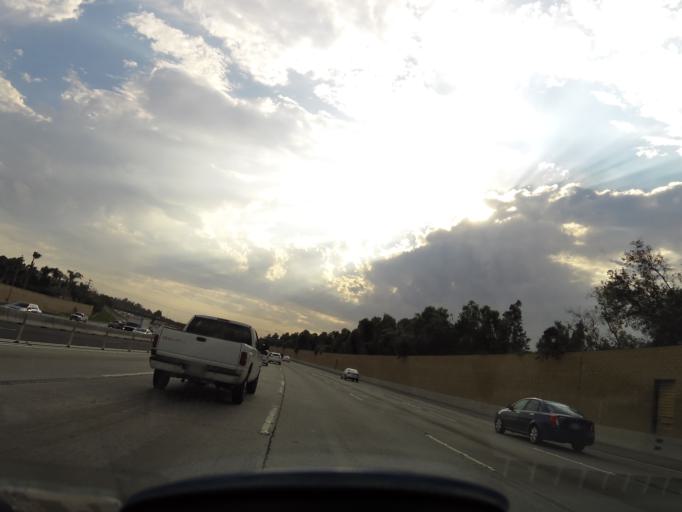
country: US
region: California
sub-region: Orange County
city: Yorba Linda
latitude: 33.8541
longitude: -117.8097
